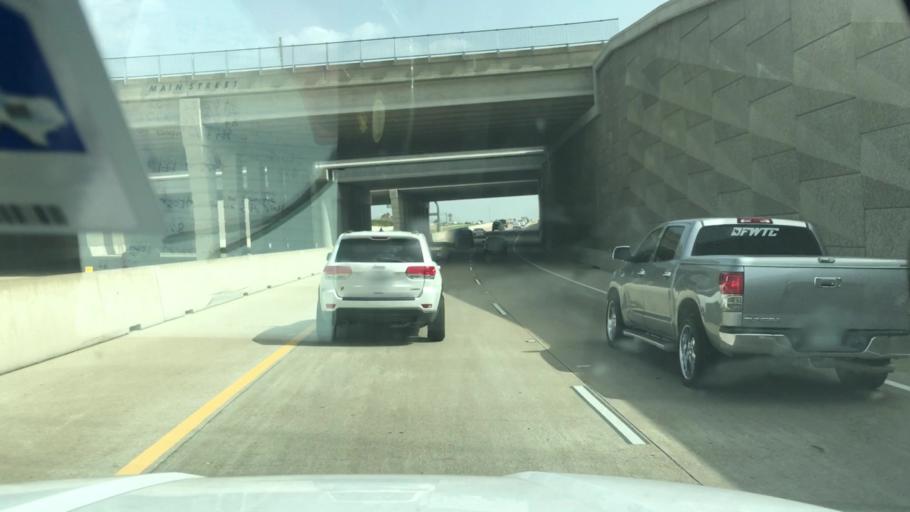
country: US
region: Texas
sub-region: Dallas County
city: Grand Prairie
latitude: 32.7422
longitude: -97.0204
